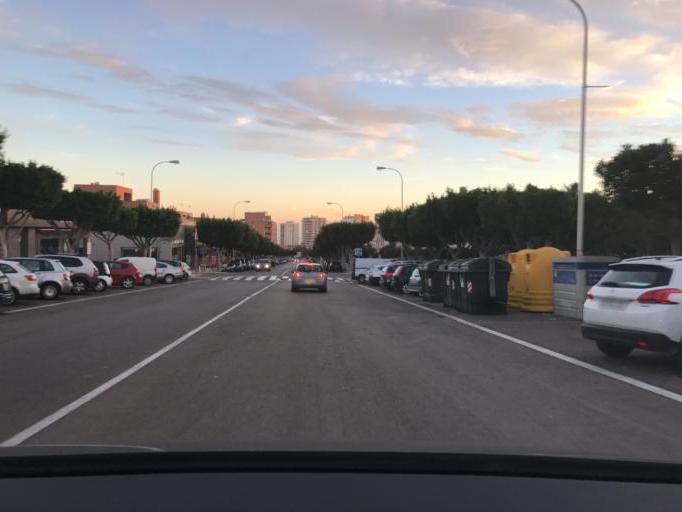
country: ES
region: Andalusia
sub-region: Provincia de Almeria
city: Aguadulce
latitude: 36.8164
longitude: -2.5806
